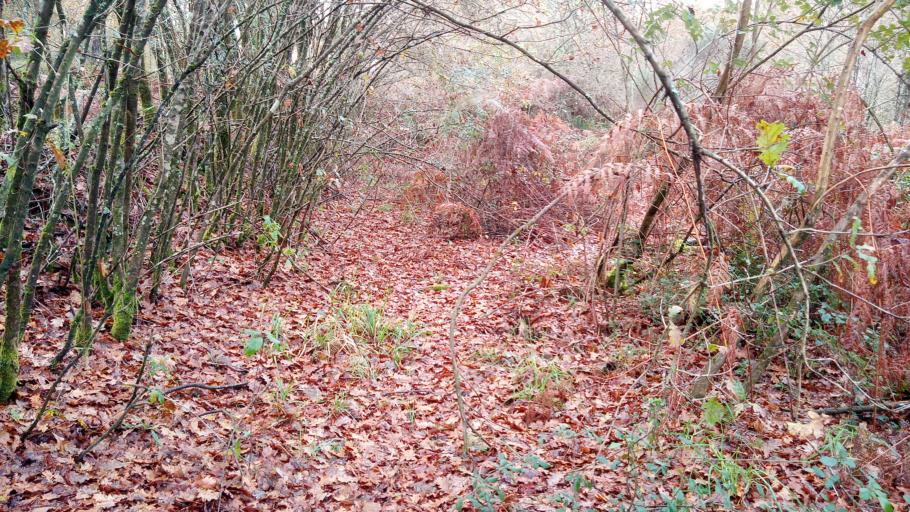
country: PT
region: Viana do Castelo
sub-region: Paredes de Coura
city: Paredes de Coura
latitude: 41.8977
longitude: -8.6160
